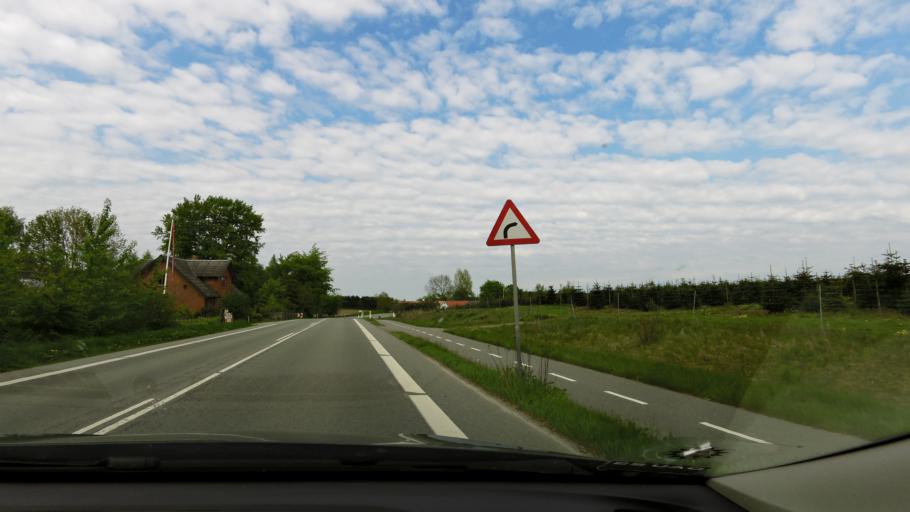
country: DK
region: South Denmark
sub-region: Nyborg Kommune
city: Ullerslev
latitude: 55.2870
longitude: 10.6951
